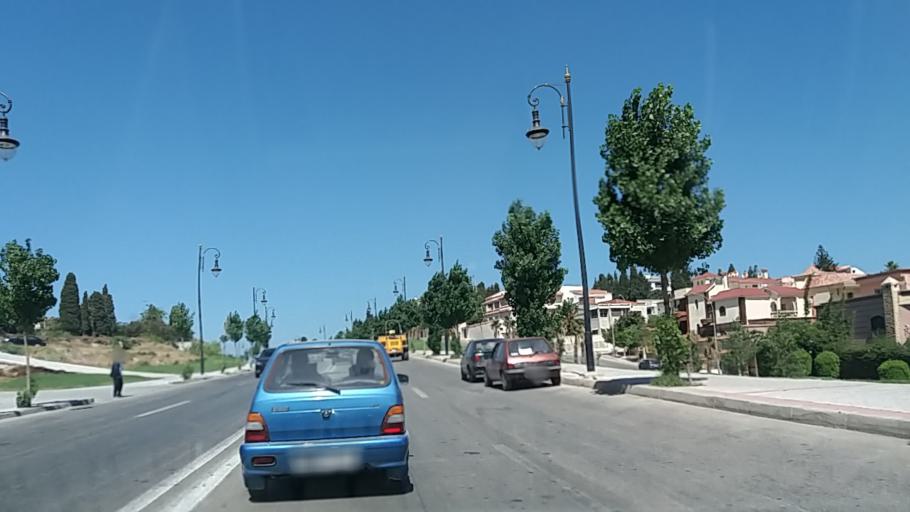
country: MA
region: Tanger-Tetouan
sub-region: Tanger-Assilah
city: Tangier
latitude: 35.7723
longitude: -5.7711
